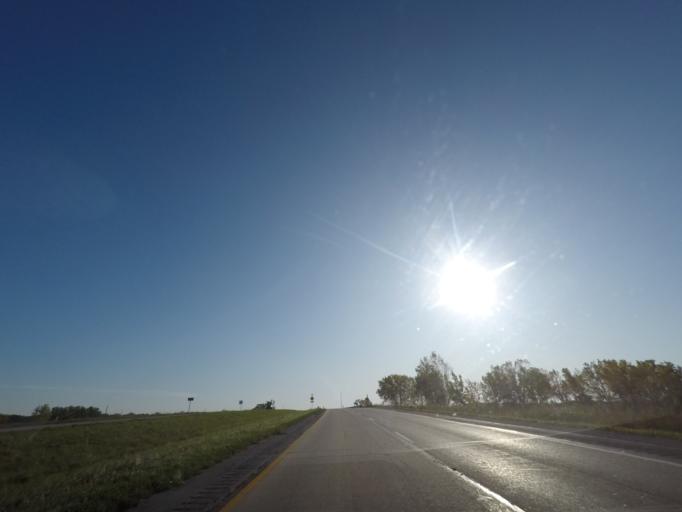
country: US
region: Iowa
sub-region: Story County
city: Nevada
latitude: 42.0066
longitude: -93.4684
